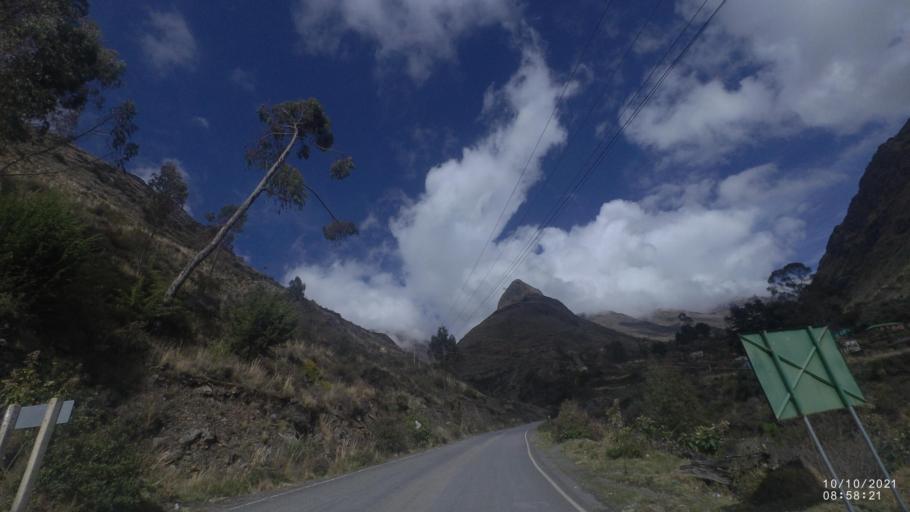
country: BO
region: La Paz
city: Quime
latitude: -16.9984
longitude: -67.2566
